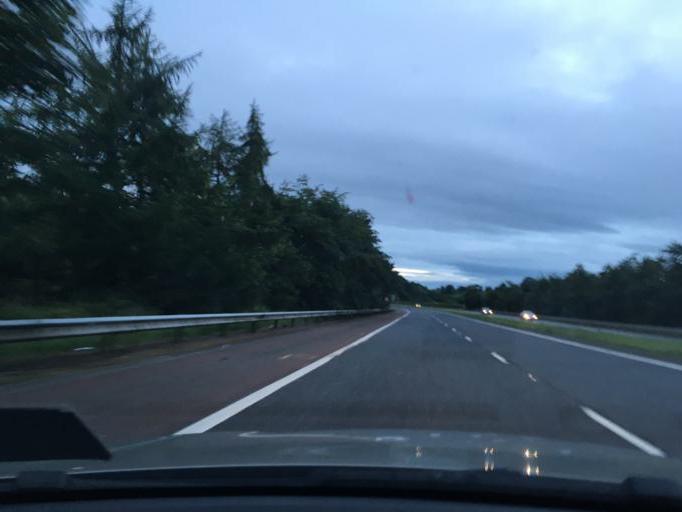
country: GB
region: Northern Ireland
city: Hillsborough
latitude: 54.4202
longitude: -6.1444
